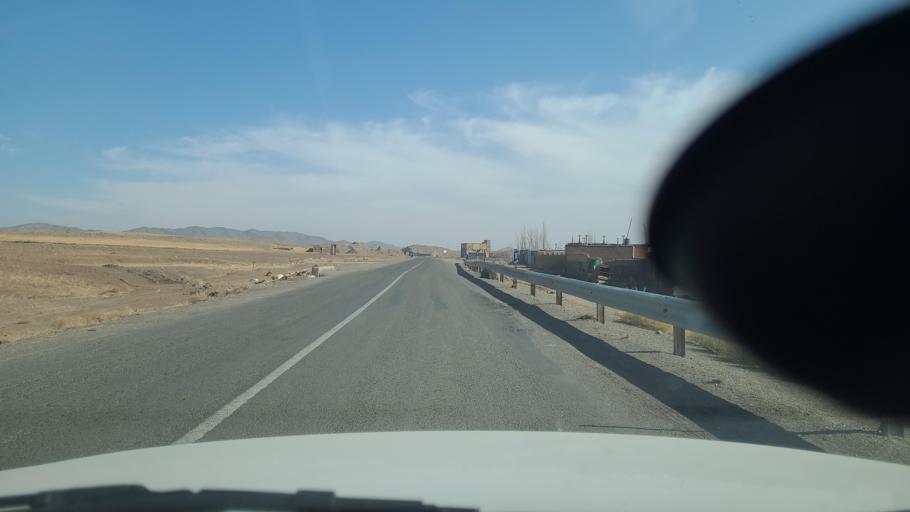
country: IR
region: Razavi Khorasan
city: Fariman
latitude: 35.5928
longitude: 59.6832
